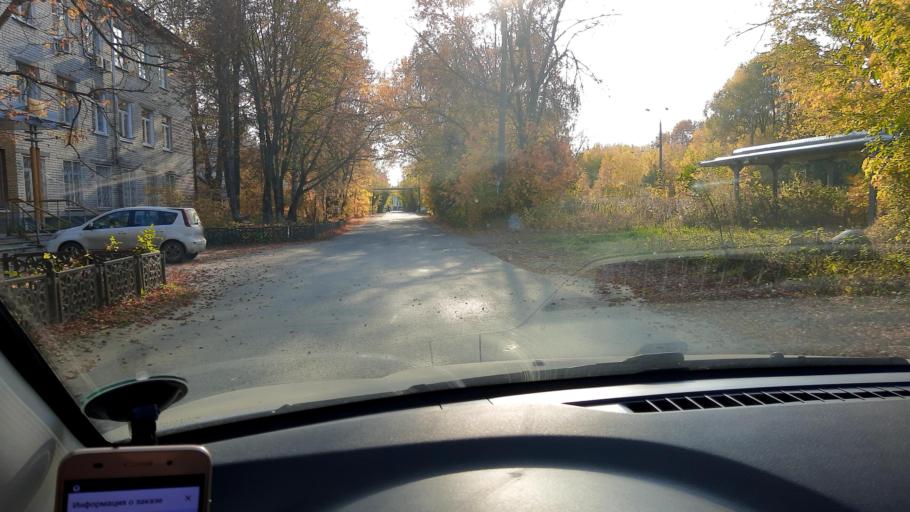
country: RU
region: Nizjnij Novgorod
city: Nizhniy Novgorod
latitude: 56.2675
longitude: 43.9333
